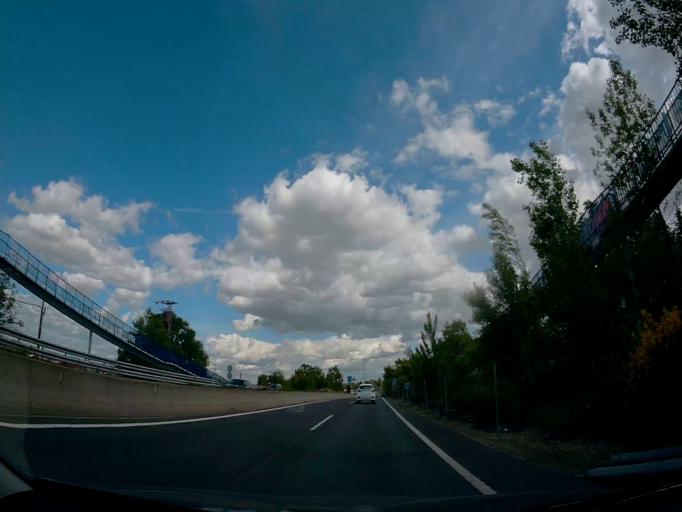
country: ES
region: Madrid
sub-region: Provincia de Madrid
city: San Sebastian de los Reyes
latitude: 40.5288
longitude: -3.6067
